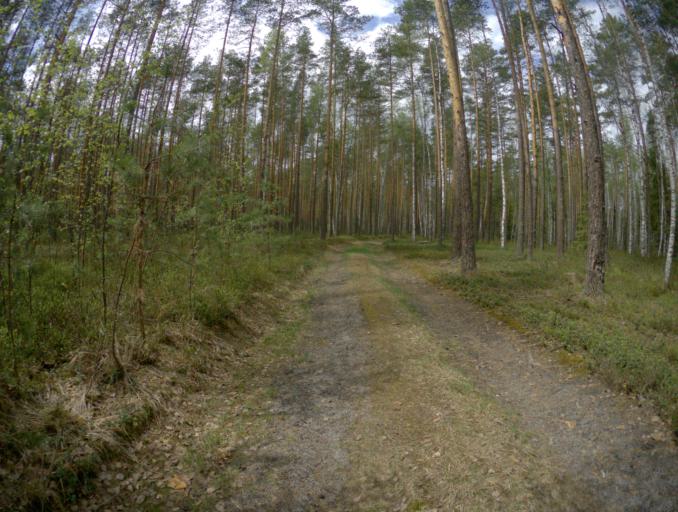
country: RU
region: Vladimir
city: Golovino
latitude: 55.9295
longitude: 40.3793
